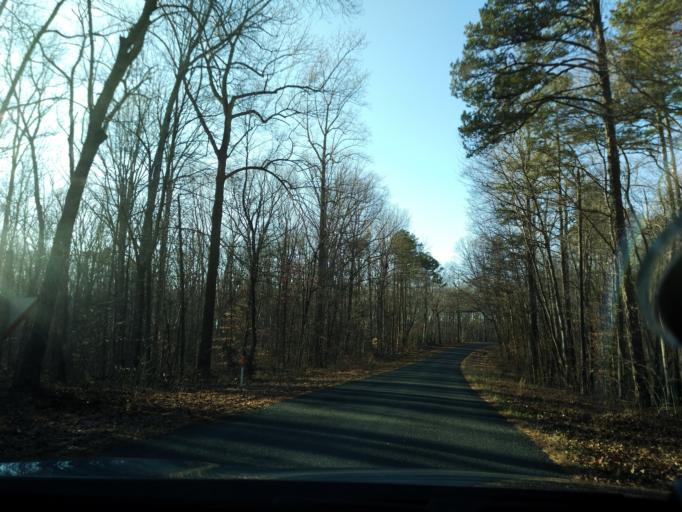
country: US
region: Virginia
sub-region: Appomattox County
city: Appomattox
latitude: 37.3952
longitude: -78.6534
